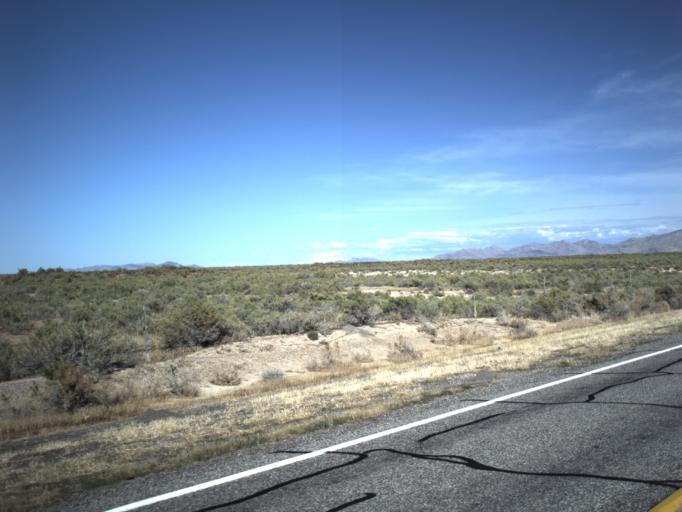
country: US
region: Utah
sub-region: Millard County
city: Delta
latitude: 39.3532
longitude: -112.5080
